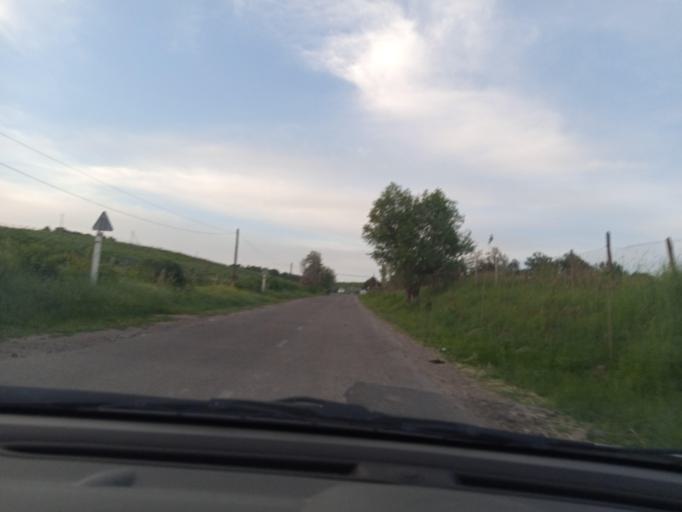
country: UZ
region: Toshkent
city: Parkent
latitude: 41.2444
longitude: 69.7324
